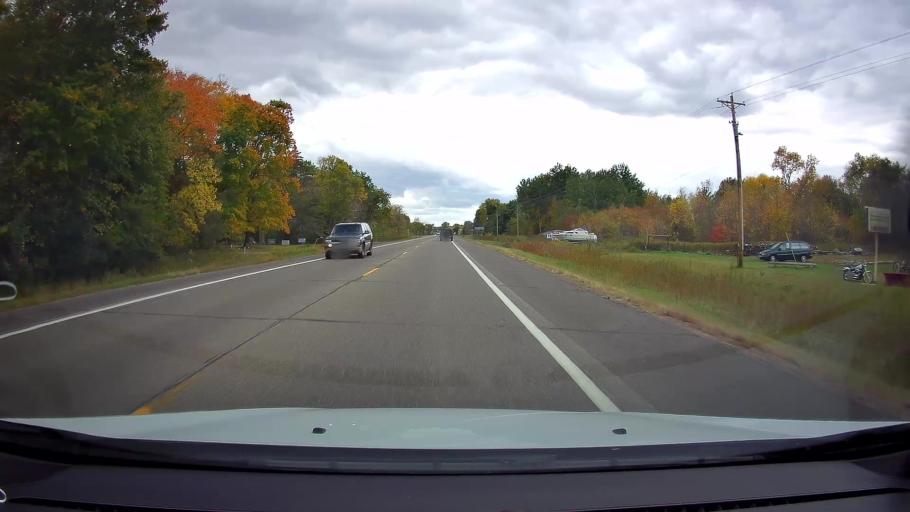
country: US
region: Minnesota
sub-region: Washington County
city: Forest Lake
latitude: 45.3056
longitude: -92.9583
